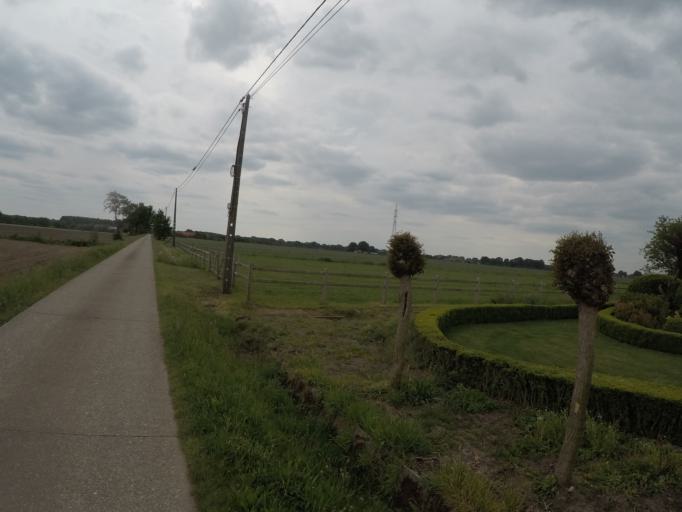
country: BE
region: Flanders
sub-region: Provincie Antwerpen
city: Oostmalle
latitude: 51.3312
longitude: 4.6900
